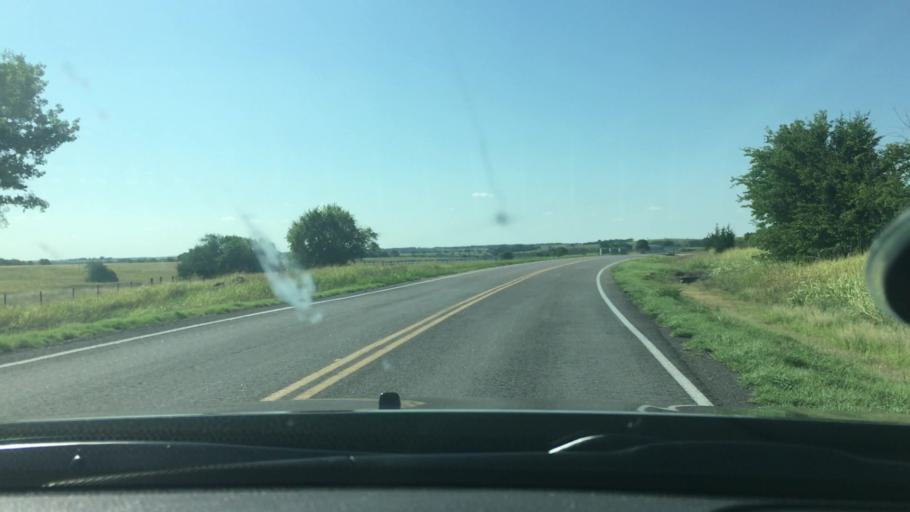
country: US
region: Oklahoma
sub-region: Johnston County
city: Tishomingo
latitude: 34.1647
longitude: -96.7076
